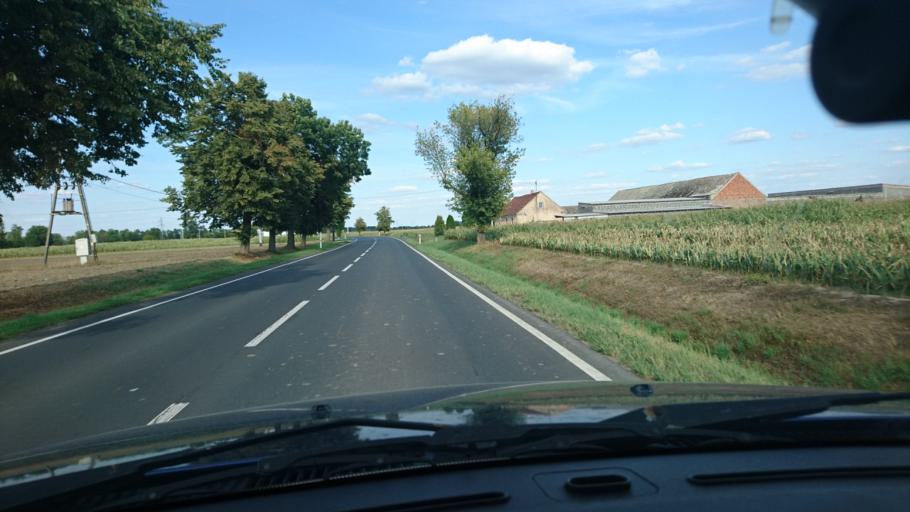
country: PL
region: Greater Poland Voivodeship
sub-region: Powiat krotoszynski
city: Kobylin
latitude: 51.7219
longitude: 17.2631
